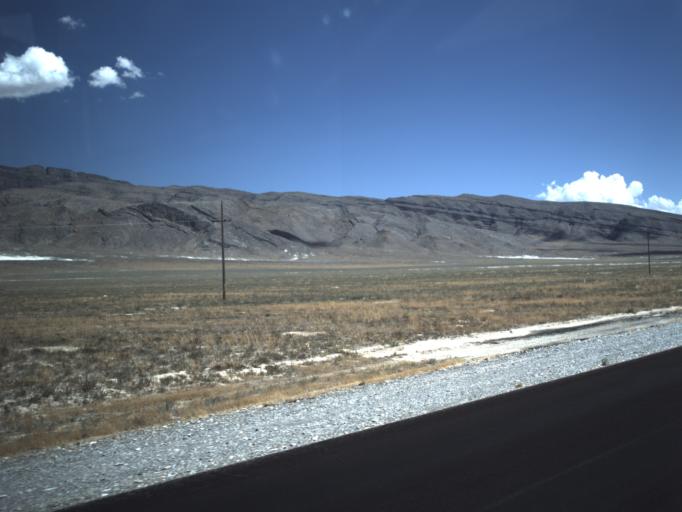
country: US
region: Utah
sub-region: Beaver County
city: Milford
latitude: 39.0708
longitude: -113.4627
